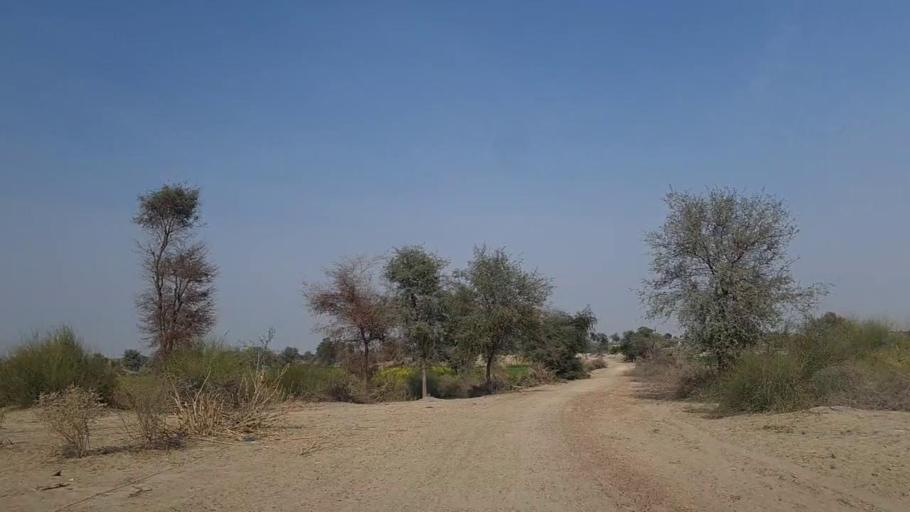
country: PK
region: Sindh
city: Daur
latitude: 26.5175
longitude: 68.4813
